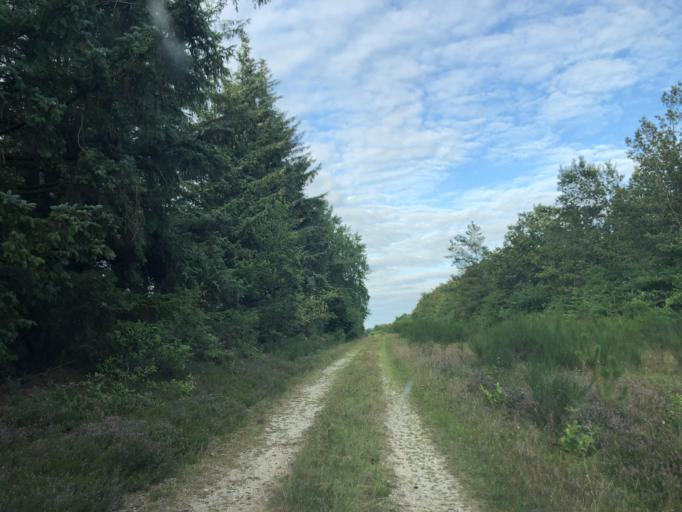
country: DK
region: Central Jutland
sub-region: Holstebro Kommune
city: Ulfborg
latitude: 56.2857
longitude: 8.4116
